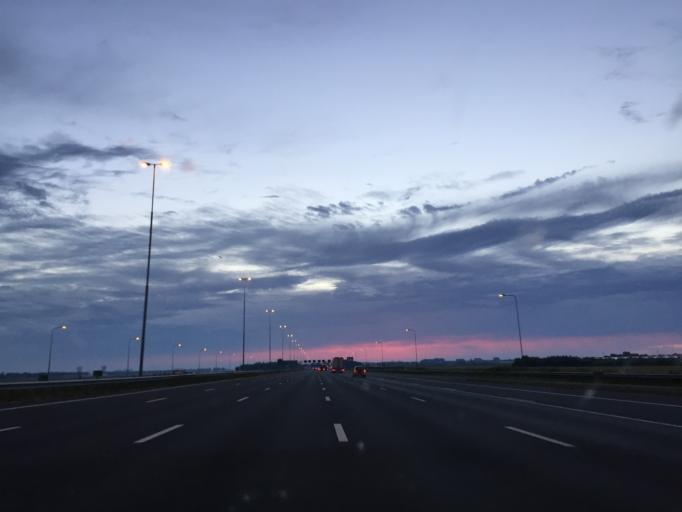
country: NL
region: South Holland
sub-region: Gemeente Kaag en Braassem
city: Leimuiden
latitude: 52.2486
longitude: 4.6703
